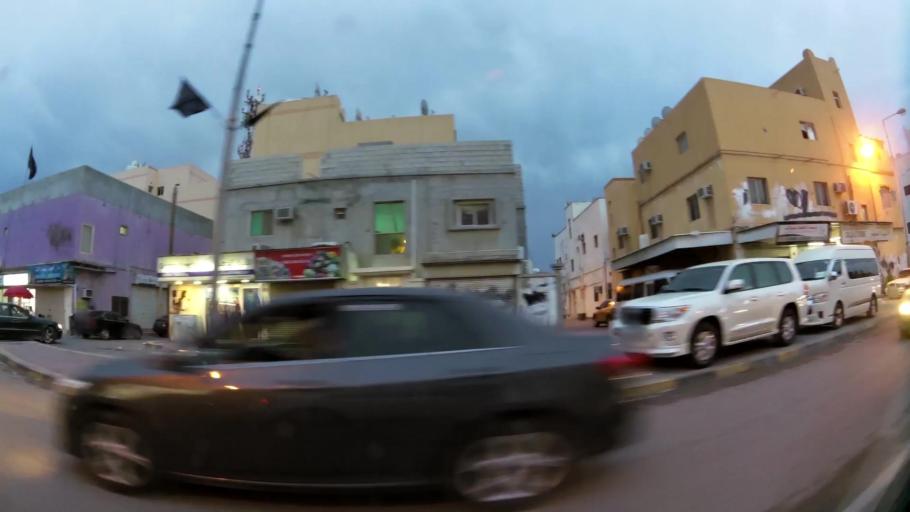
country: BH
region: Central Governorate
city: Madinat Hamad
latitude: 26.1459
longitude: 50.4985
